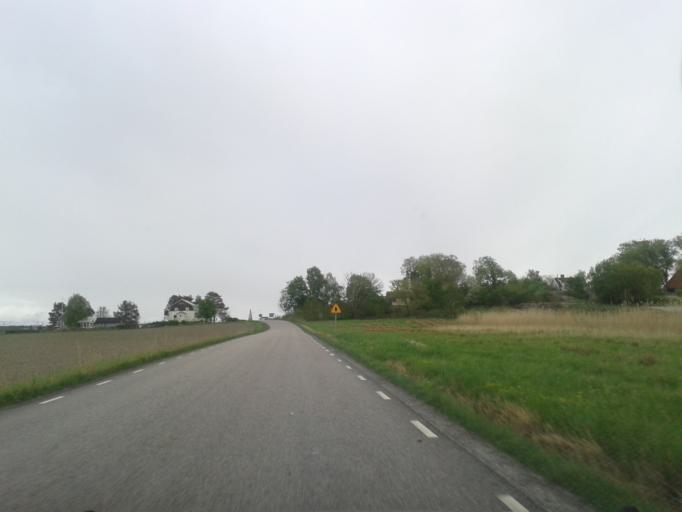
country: SE
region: Vaestra Goetaland
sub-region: Kungalvs Kommun
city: Kode
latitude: 57.9429
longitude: 11.8201
